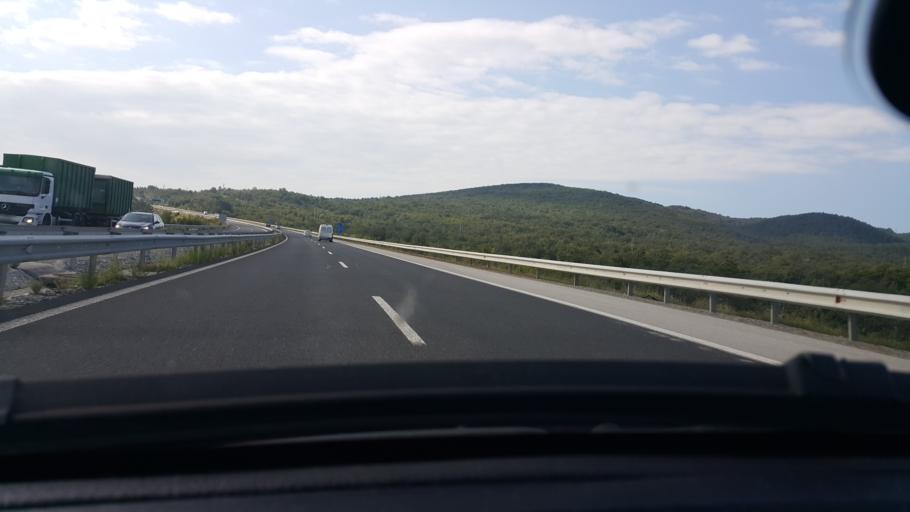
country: SI
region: Divaca
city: Divaca
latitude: 45.6524
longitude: 13.9608
